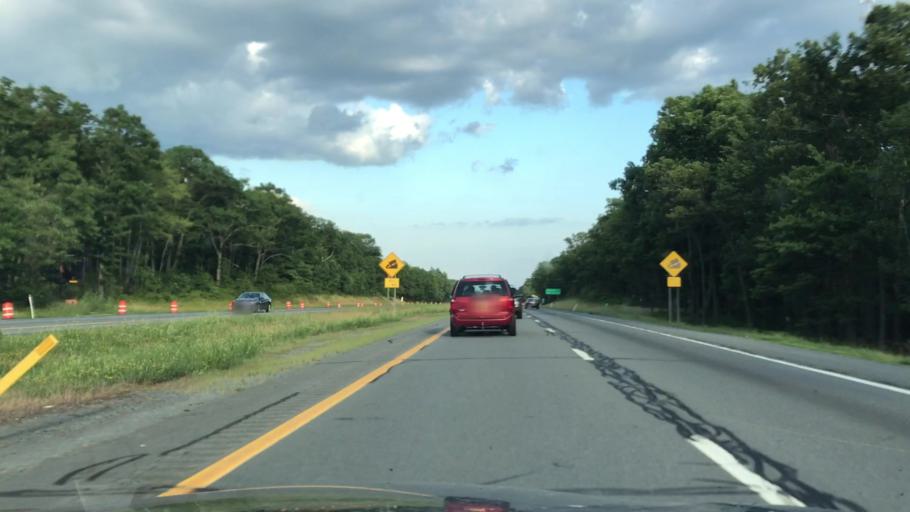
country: US
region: New York
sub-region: Sullivan County
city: Rock Hill
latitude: 41.6027
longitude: -74.5563
